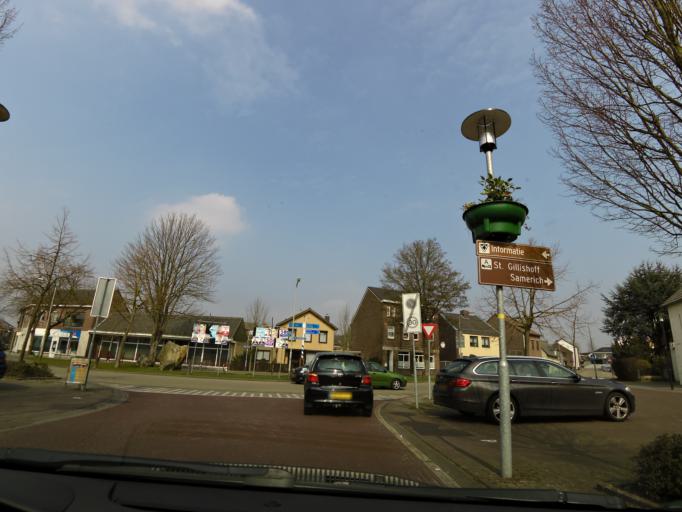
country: NL
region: Limburg
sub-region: Gemeente Simpelveld
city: Simpelveld
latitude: 50.8192
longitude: 6.0090
